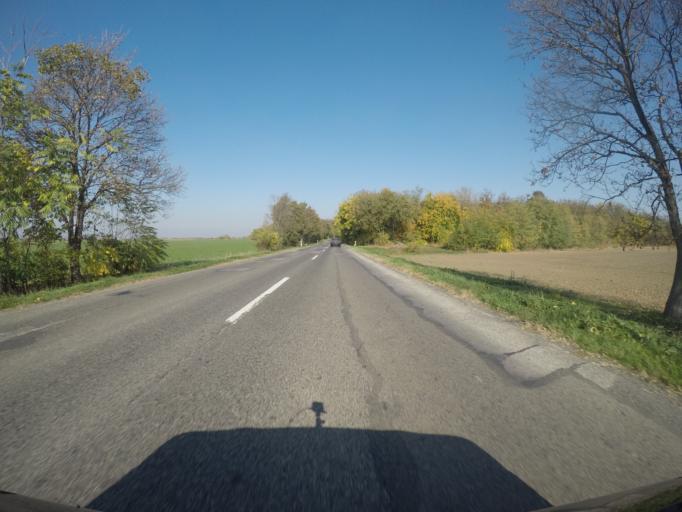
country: HU
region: Tolna
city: Szedres
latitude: 46.4564
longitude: 18.6870
